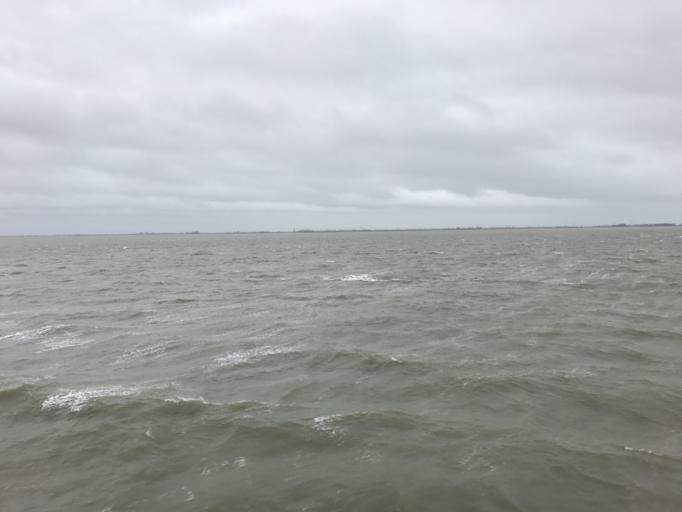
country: NL
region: Groningen
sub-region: Gemeente Delfzijl
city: Delfzijl
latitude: 53.4217
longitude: 6.9278
